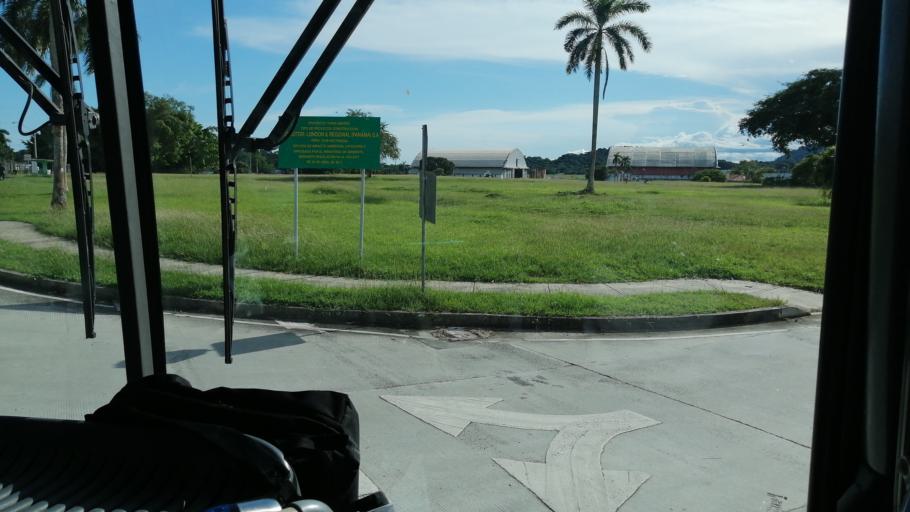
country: PA
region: Panama
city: Veracruz
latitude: 8.9171
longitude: -79.5921
